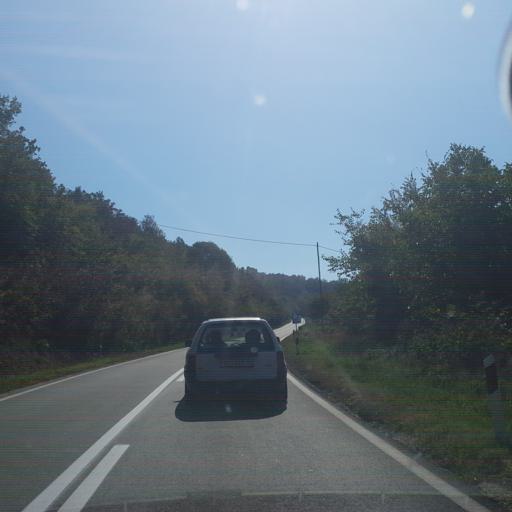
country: RS
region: Central Serbia
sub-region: Zajecarski Okrug
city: Knjazevac
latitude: 43.5441
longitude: 22.2329
